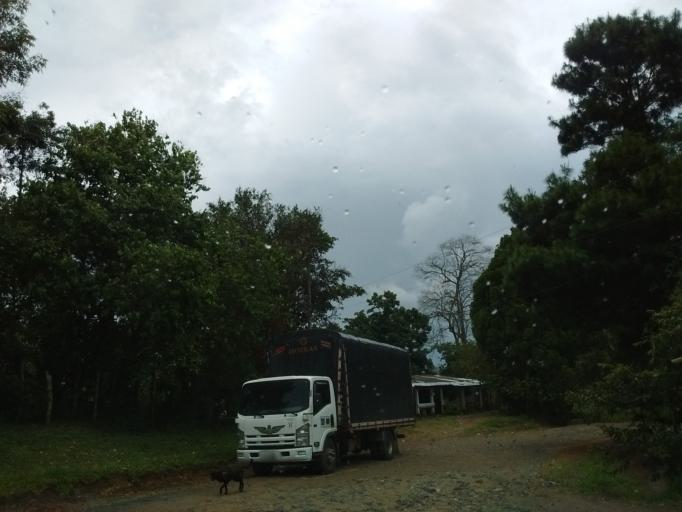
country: CO
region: Cauca
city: Cajibio
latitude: 2.5670
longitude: -76.6360
